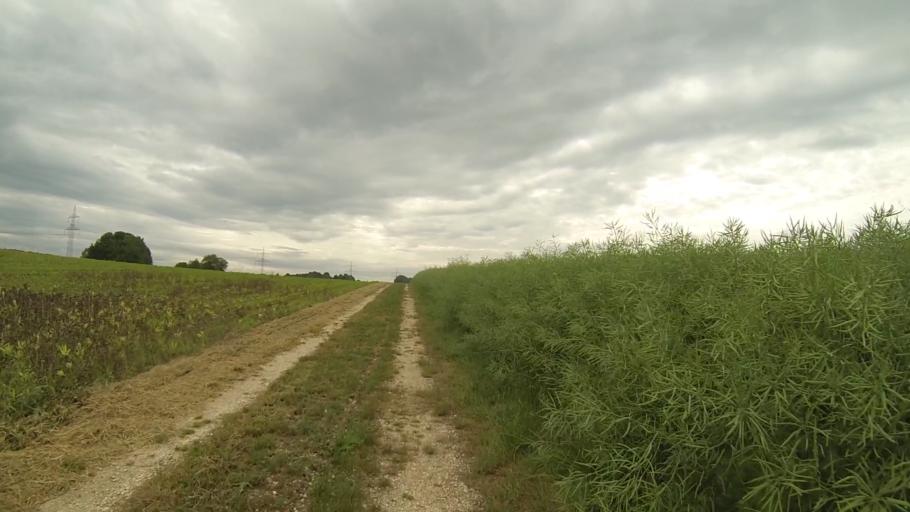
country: DE
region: Baden-Wuerttemberg
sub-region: Tuebingen Region
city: Blaubeuren
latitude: 48.4298
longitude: 9.7902
